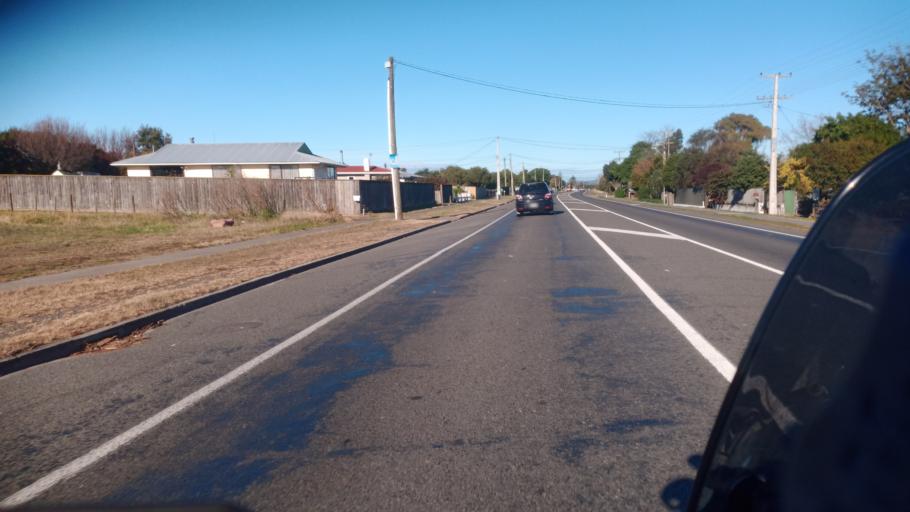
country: NZ
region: Hawke's Bay
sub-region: Napier City
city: Napier
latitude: -39.4306
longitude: 176.8718
